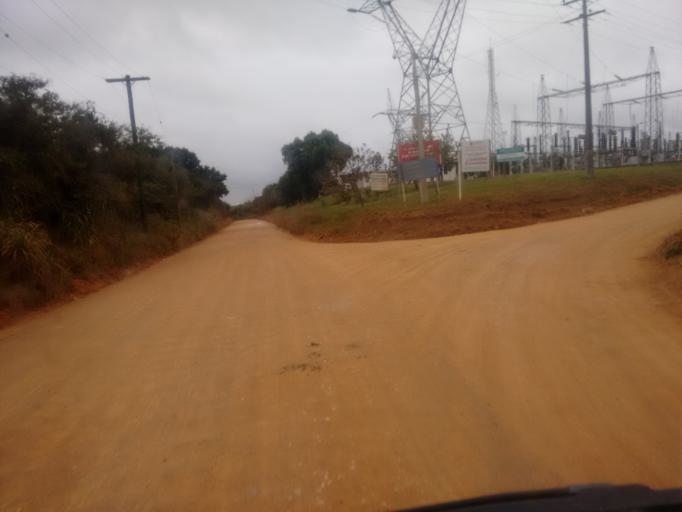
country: BR
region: Rio Grande do Sul
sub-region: Camaqua
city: Camaqua
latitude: -30.8281
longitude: -51.8173
